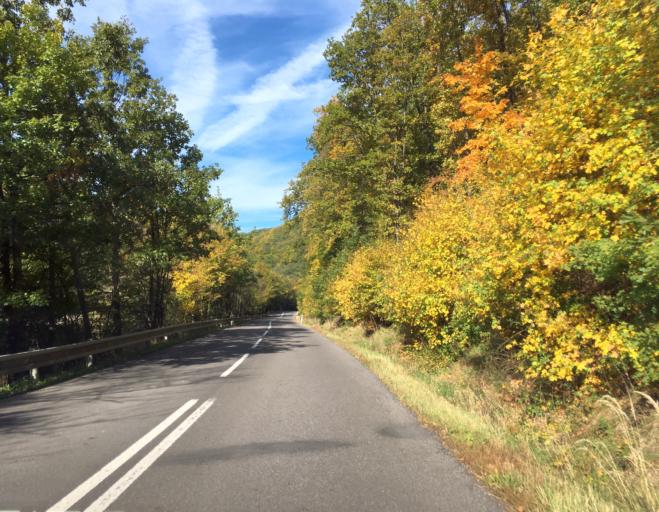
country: SK
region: Banskobystricky
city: Krupina
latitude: 48.3085
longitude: 18.9744
